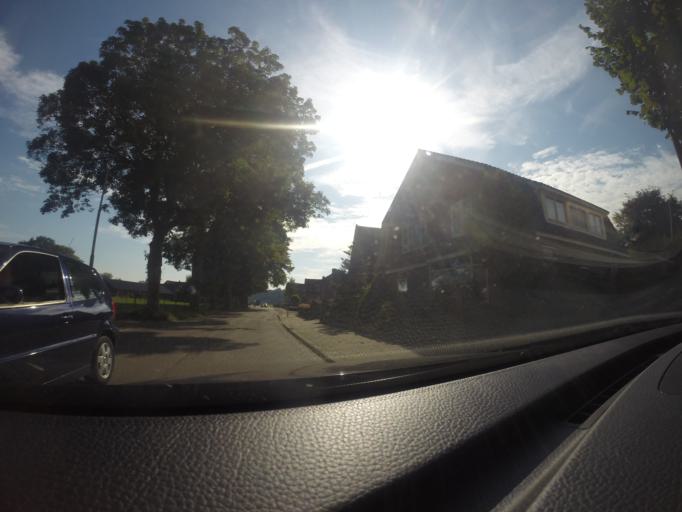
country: NL
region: Gelderland
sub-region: Oude IJsselstreek
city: Wisch
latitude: 51.9384
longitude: 6.3508
